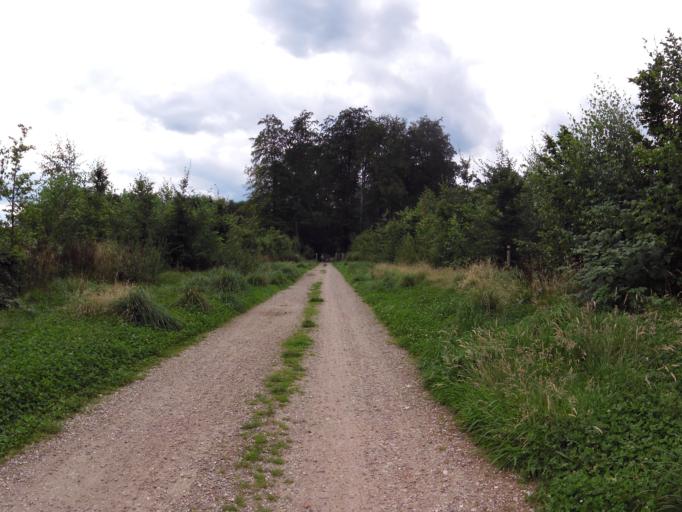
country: NL
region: Gelderland
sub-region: Gemeente Rheden
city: Ellecom
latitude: 52.0399
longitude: 6.0918
